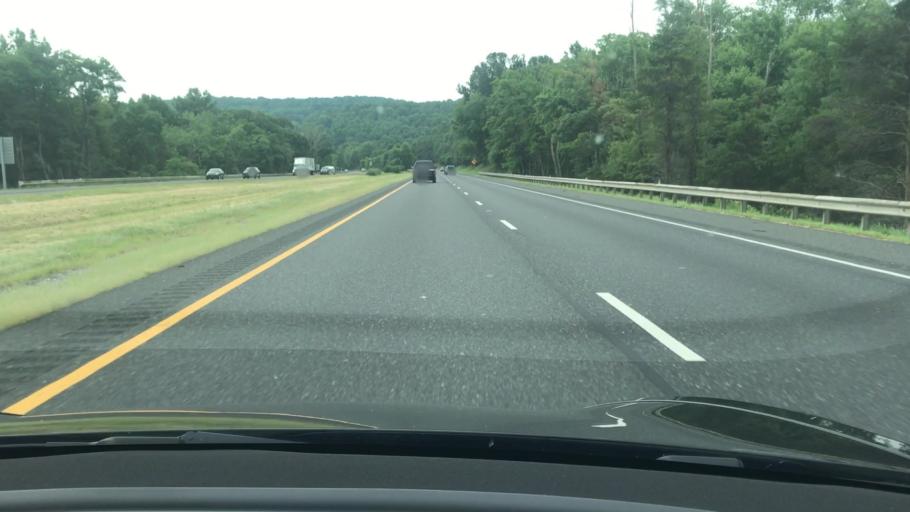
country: US
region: Maryland
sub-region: Baltimore County
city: Hunt Valley
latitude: 39.6197
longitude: -76.6659
